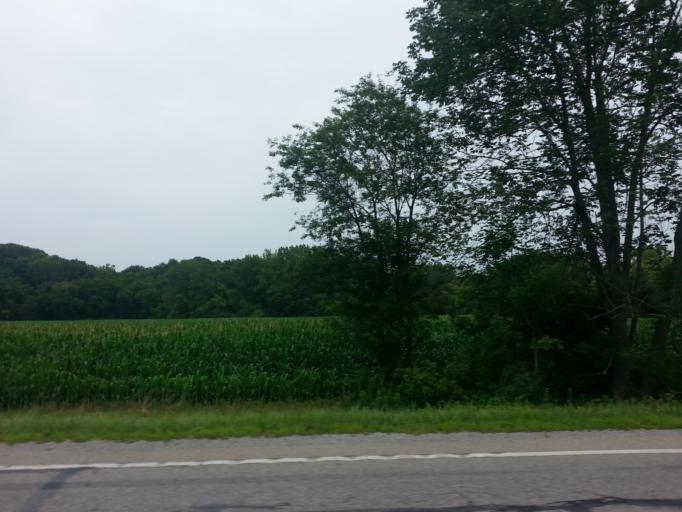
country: US
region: Ohio
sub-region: Brown County
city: Mount Orab
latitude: 38.9525
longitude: -83.9100
